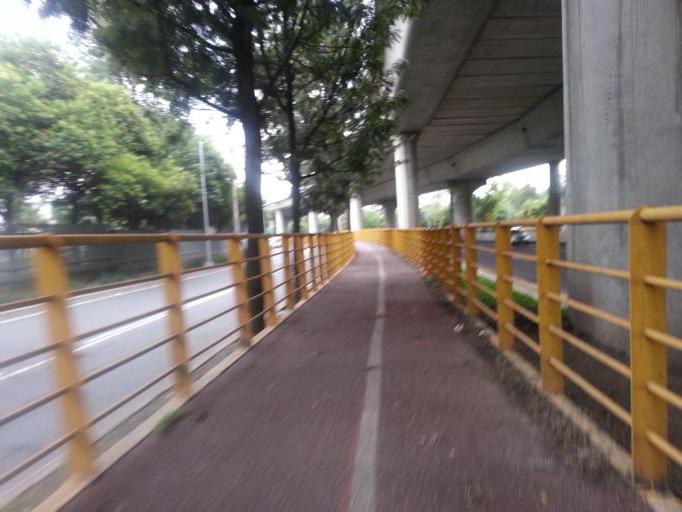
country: MX
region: Mexico City
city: Polanco
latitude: 19.4135
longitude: -99.1936
